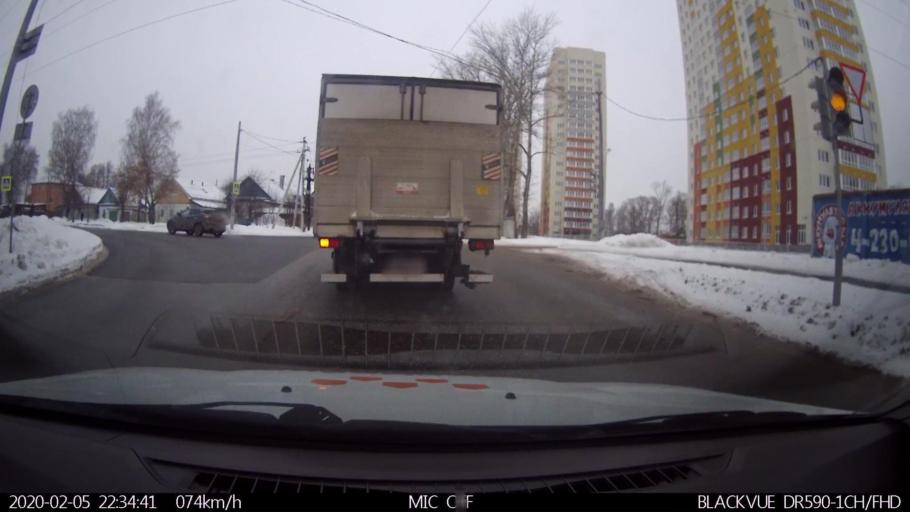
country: RU
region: Nizjnij Novgorod
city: Imeni Stepana Razina
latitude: 54.7355
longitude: 44.2280
